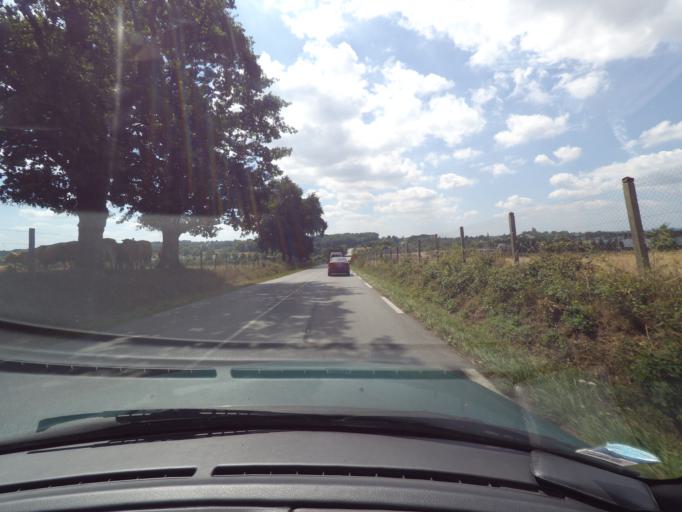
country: FR
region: Limousin
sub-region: Departement de la Haute-Vienne
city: Limoges
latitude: 45.7976
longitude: 1.2513
